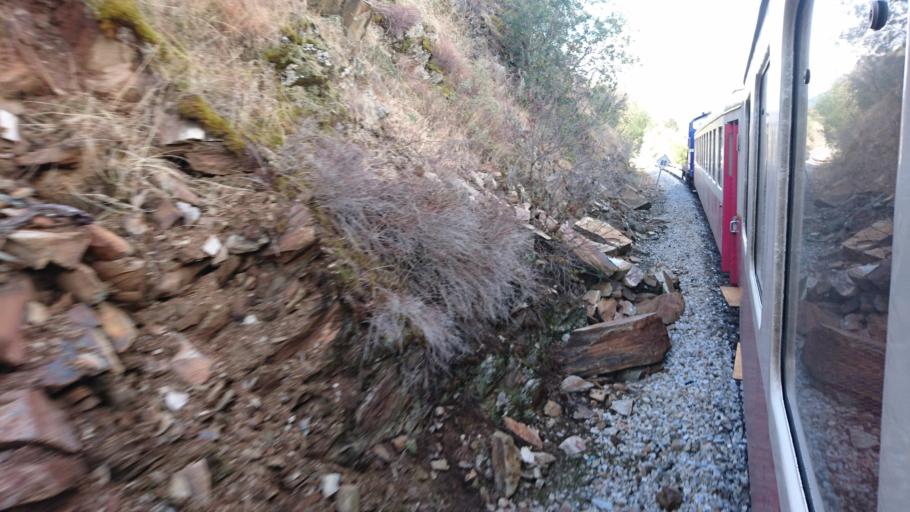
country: PT
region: Guarda
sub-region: Vila Nova de Foz Coa
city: Vila Nova de Foz Coa
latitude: 41.1435
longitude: -7.2492
